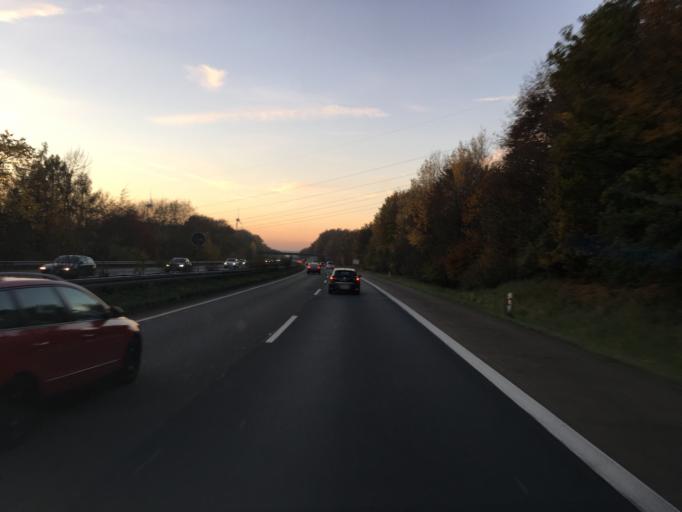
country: DE
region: North Rhine-Westphalia
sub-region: Regierungsbezirk Arnsberg
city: Nachrodt-Wiblingwerde
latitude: 51.3167
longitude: 7.5497
